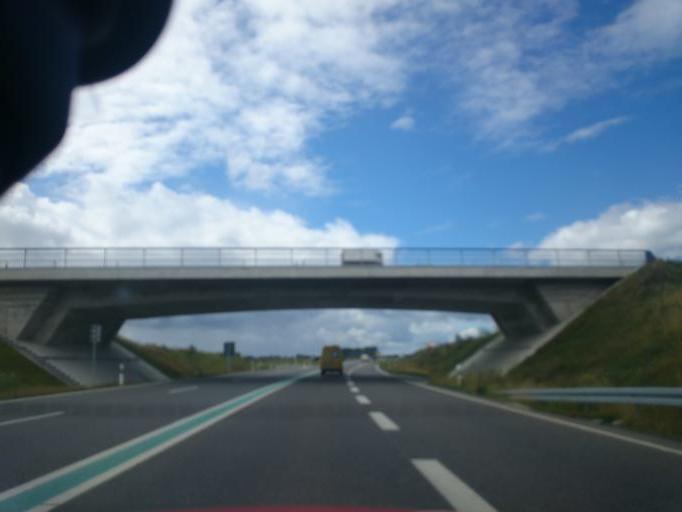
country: DE
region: Mecklenburg-Vorpommern
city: Samtens
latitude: 54.3506
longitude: 13.2991
